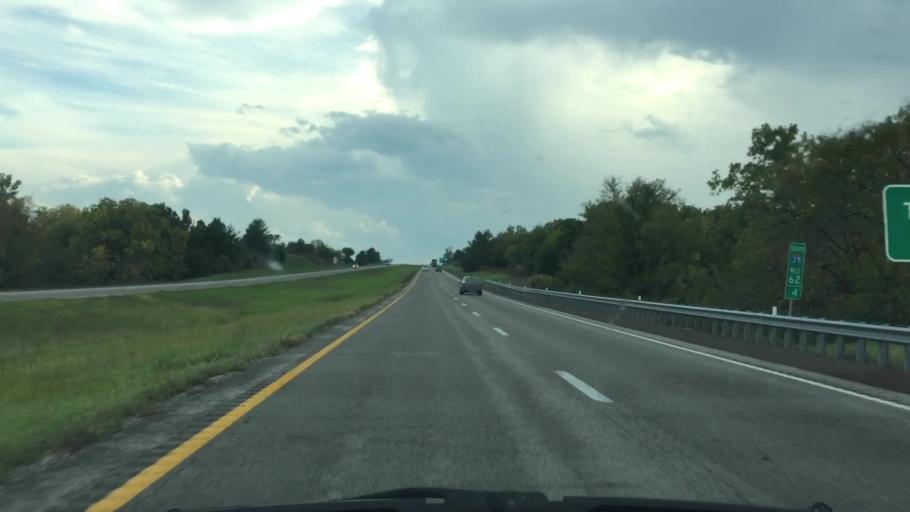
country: US
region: Missouri
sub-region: Clinton County
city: Cameron
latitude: 39.8662
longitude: -94.1713
